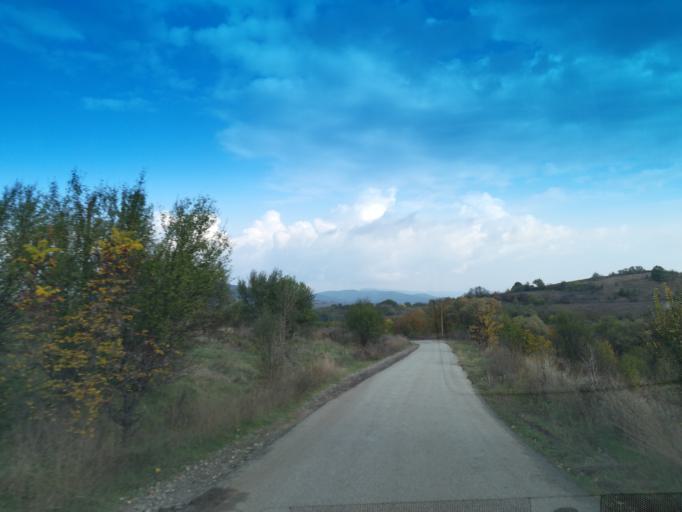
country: BG
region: Stara Zagora
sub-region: Obshtina Nikolaevo
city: Elkhovo
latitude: 42.3352
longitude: 25.4055
